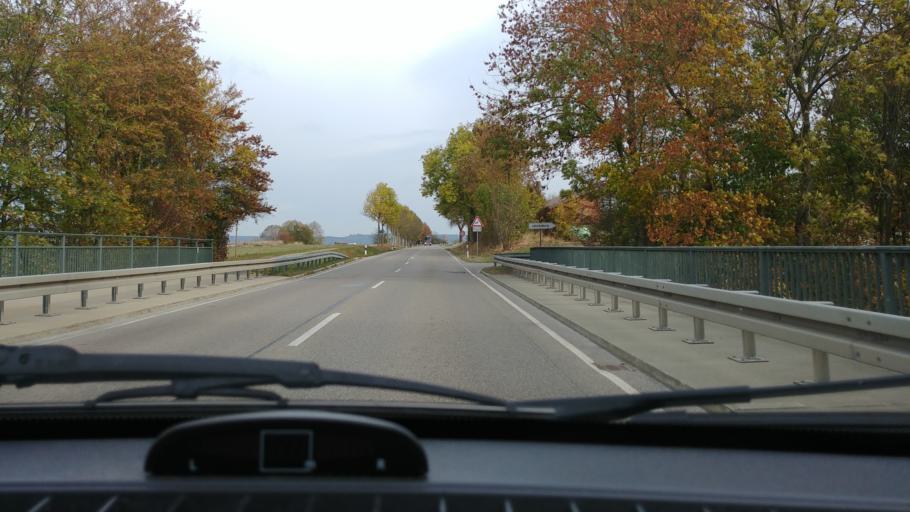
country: DE
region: Baden-Wuerttemberg
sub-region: Regierungsbezirk Stuttgart
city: Crailsheim
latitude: 49.1024
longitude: 10.0689
